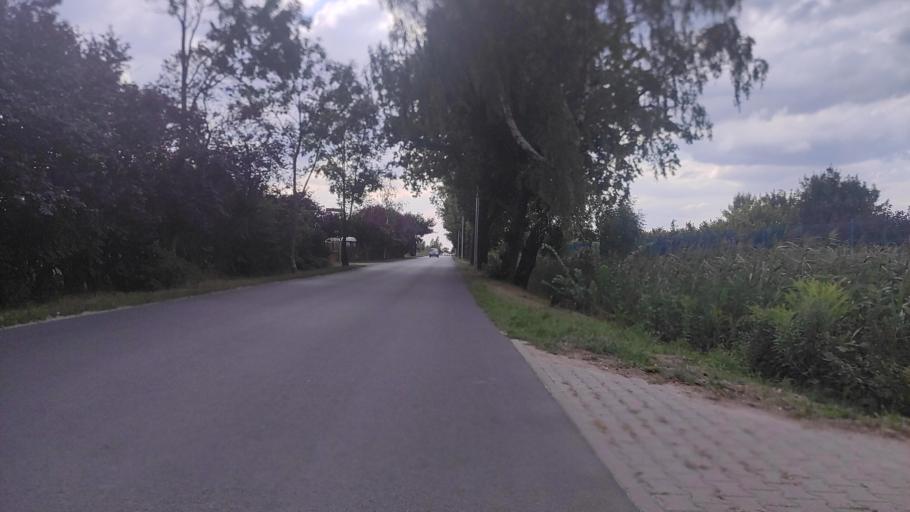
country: PL
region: Greater Poland Voivodeship
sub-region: Powiat poznanski
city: Swarzedz
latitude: 52.3875
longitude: 17.1007
